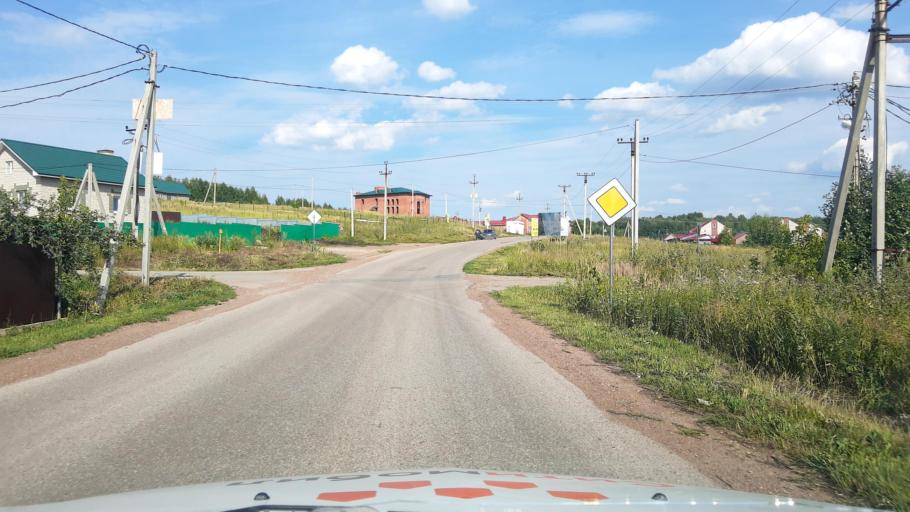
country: RU
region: Bashkortostan
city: Kabakovo
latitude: 54.6668
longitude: 56.2118
